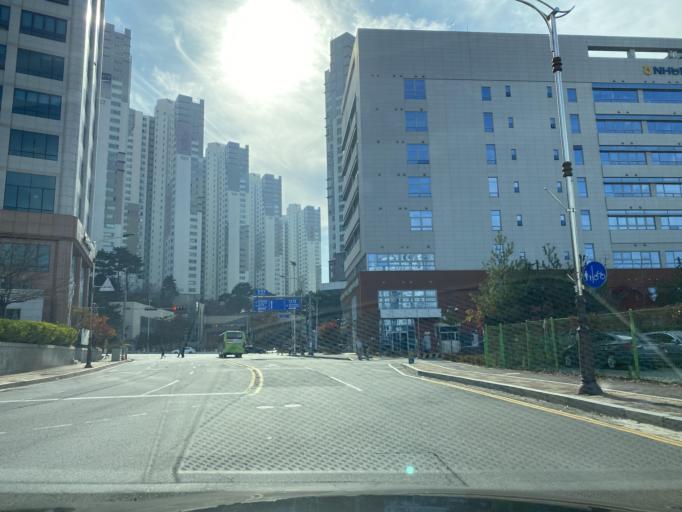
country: KR
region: Chungcheongnam-do
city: Cheonan
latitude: 36.7984
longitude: 127.1079
